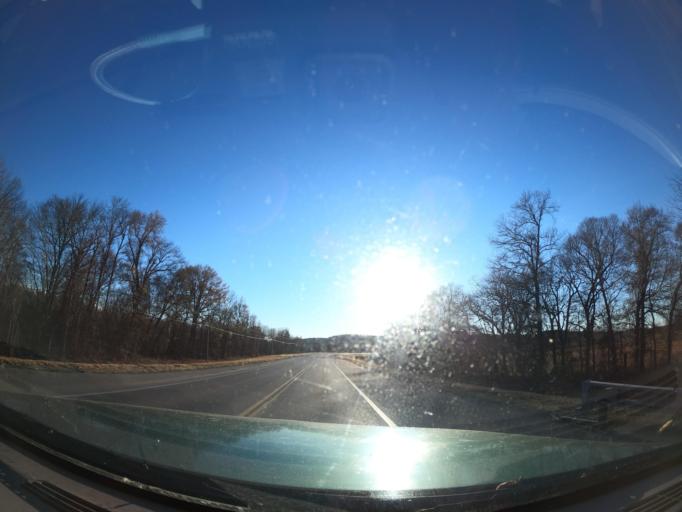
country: US
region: Oklahoma
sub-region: Pittsburg County
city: Hartshorne
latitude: 34.8948
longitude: -95.4378
